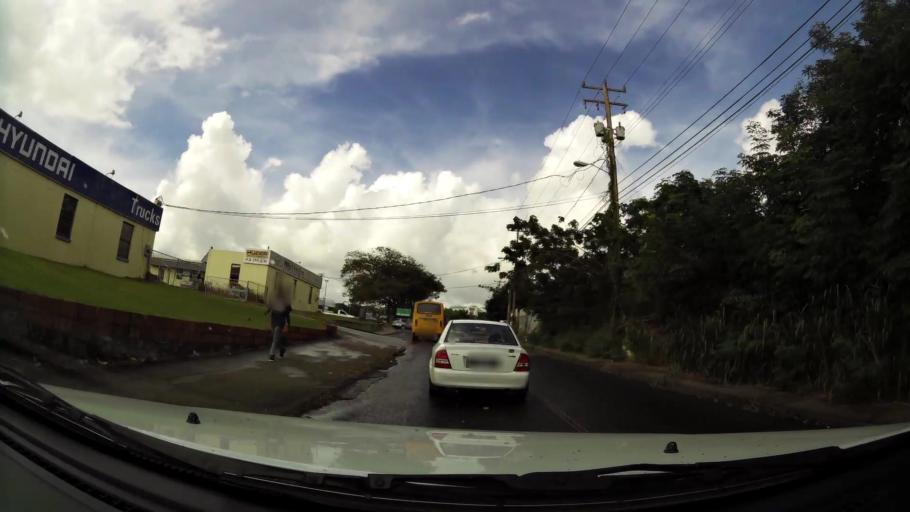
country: BB
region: Saint Michael
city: Bridgetown
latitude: 13.1397
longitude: -59.6066
